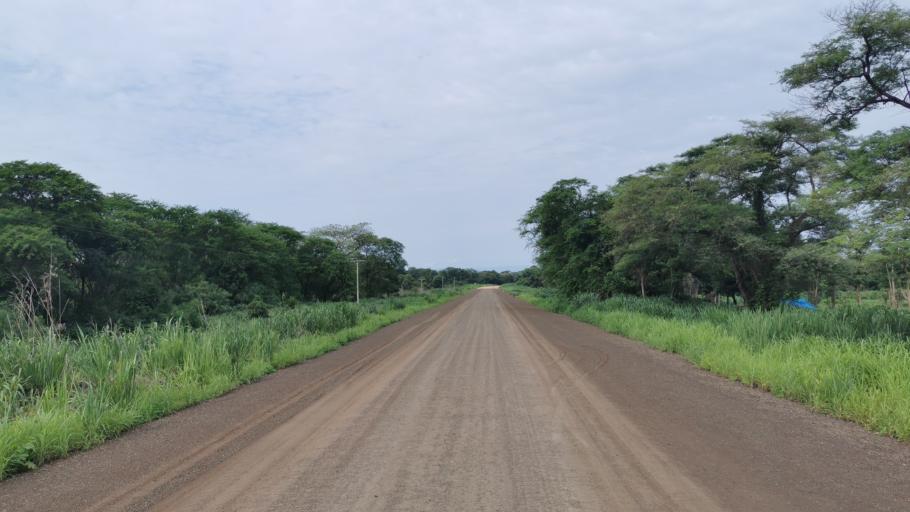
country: ET
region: Gambela
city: Gambela
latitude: 7.8328
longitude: 34.5181
